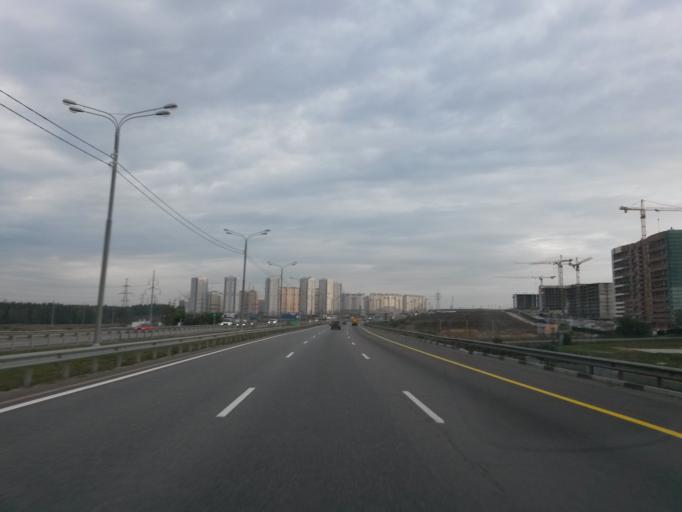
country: RU
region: Moskovskaya
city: Vostryakovo
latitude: 55.3841
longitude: 37.7769
